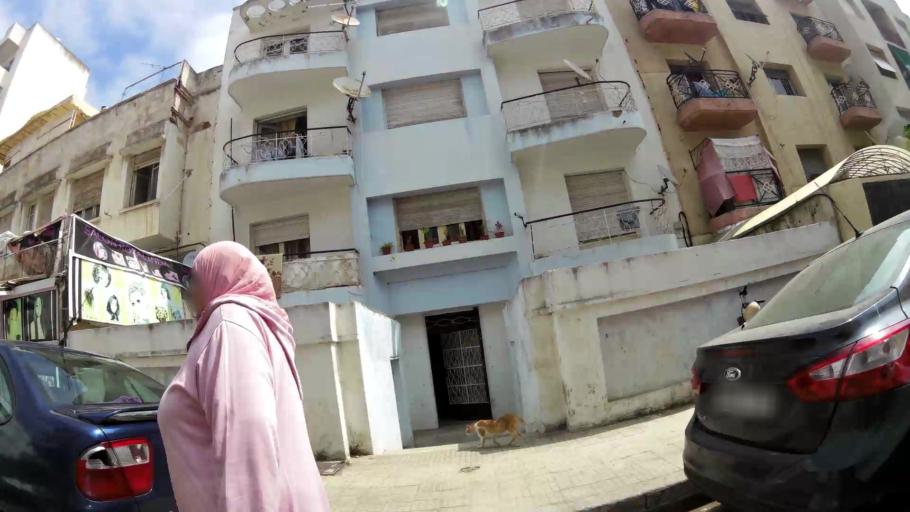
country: MA
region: Rabat-Sale-Zemmour-Zaer
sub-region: Rabat
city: Rabat
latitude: 34.0148
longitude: -6.8486
